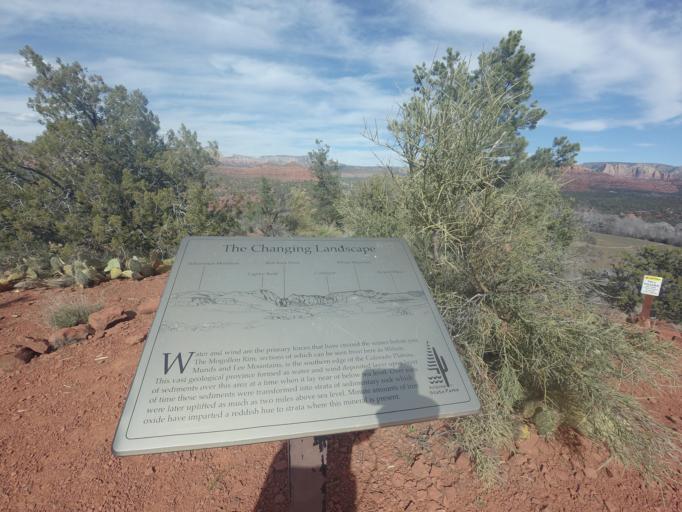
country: US
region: Arizona
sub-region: Yavapai County
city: West Sedona
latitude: 34.8104
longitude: -111.8324
